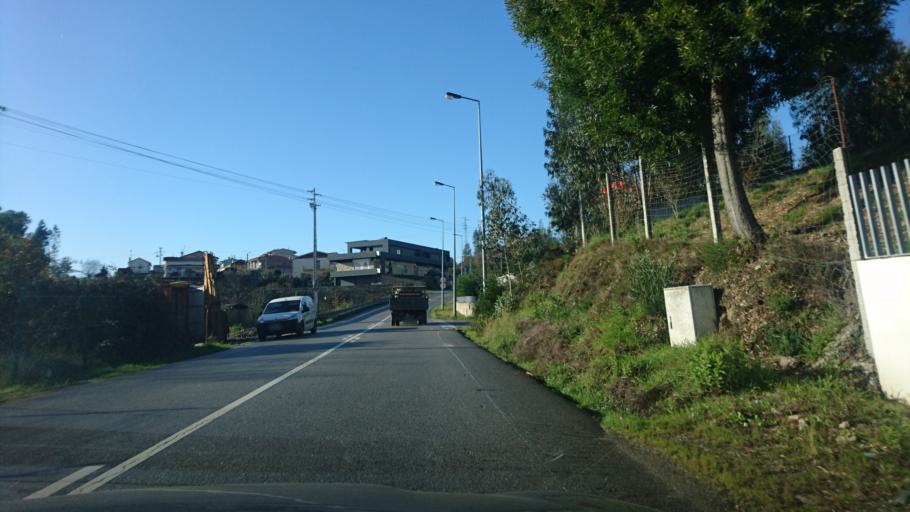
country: PT
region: Porto
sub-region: Paredes
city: Recarei
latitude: 41.1505
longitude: -8.3992
